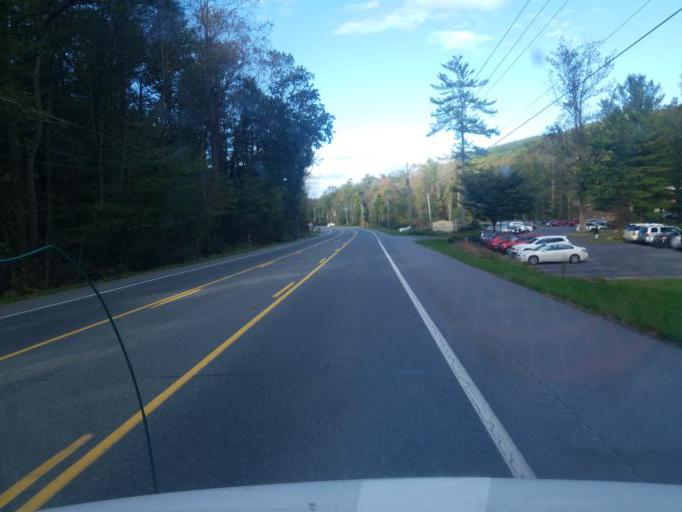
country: US
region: Pennsylvania
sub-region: Franklin County
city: Fayetteville
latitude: 39.8994
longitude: -77.4410
